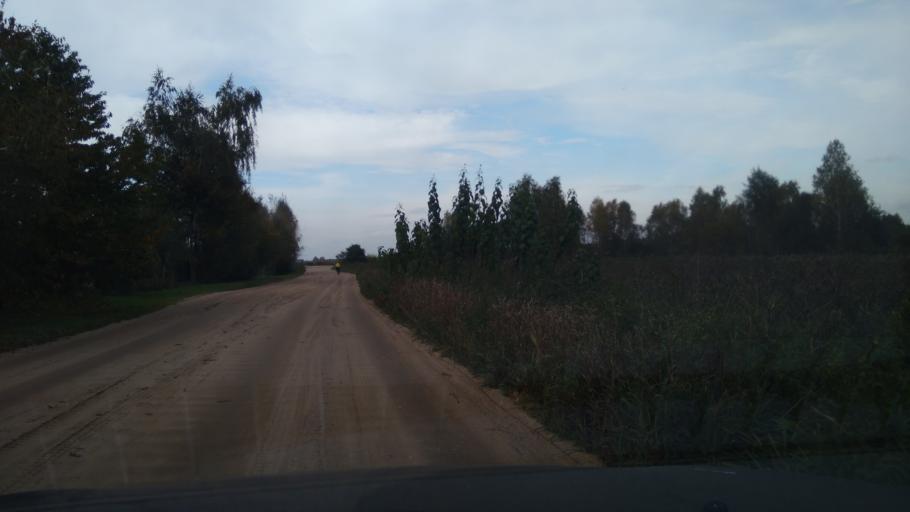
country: BY
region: Minsk
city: Rudzyensk
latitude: 53.6130
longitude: 27.8466
